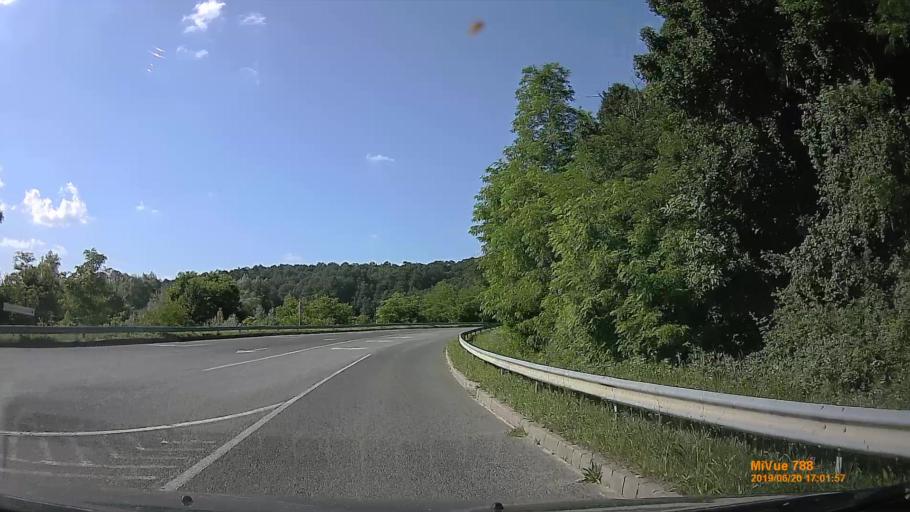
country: HU
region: Baranya
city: Buekkoesd
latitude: 46.1249
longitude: 18.0252
